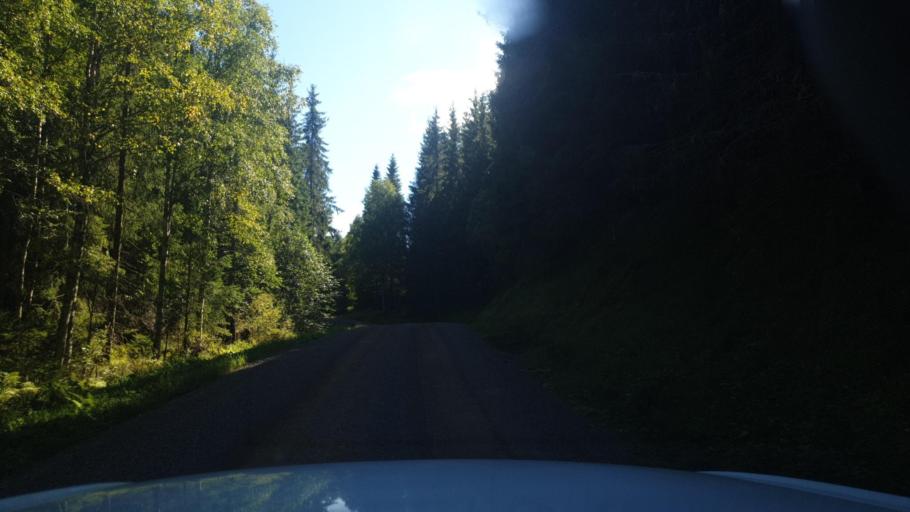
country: SE
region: Vaermland
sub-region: Eda Kommun
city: Charlottenberg
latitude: 60.0648
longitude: 12.5415
